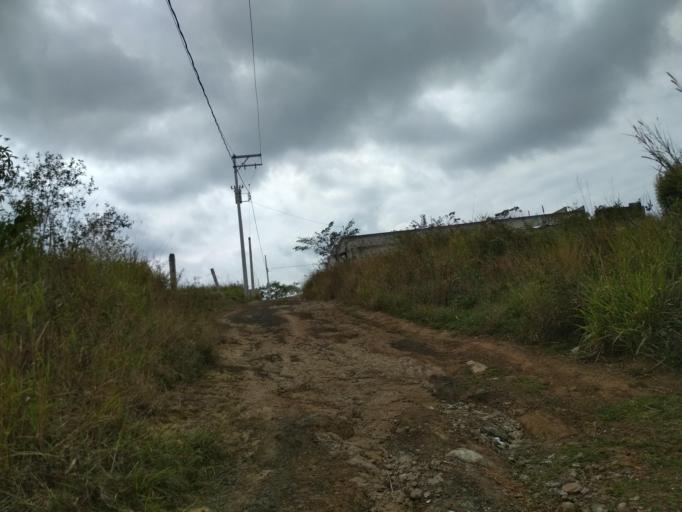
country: MX
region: Veracruz
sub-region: Emiliano Zapata
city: Jacarandas
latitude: 19.4971
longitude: -96.8360
